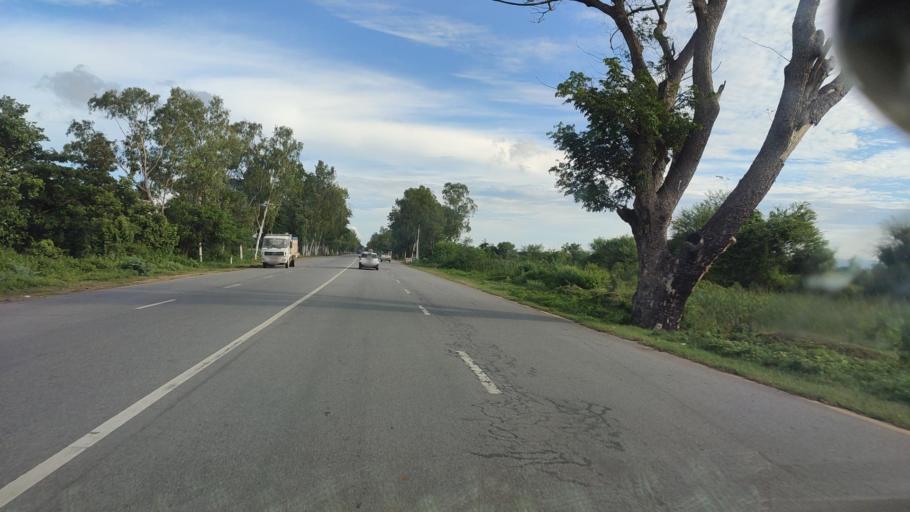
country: MM
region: Mandalay
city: Yamethin
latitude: 20.1713
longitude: 96.1887
